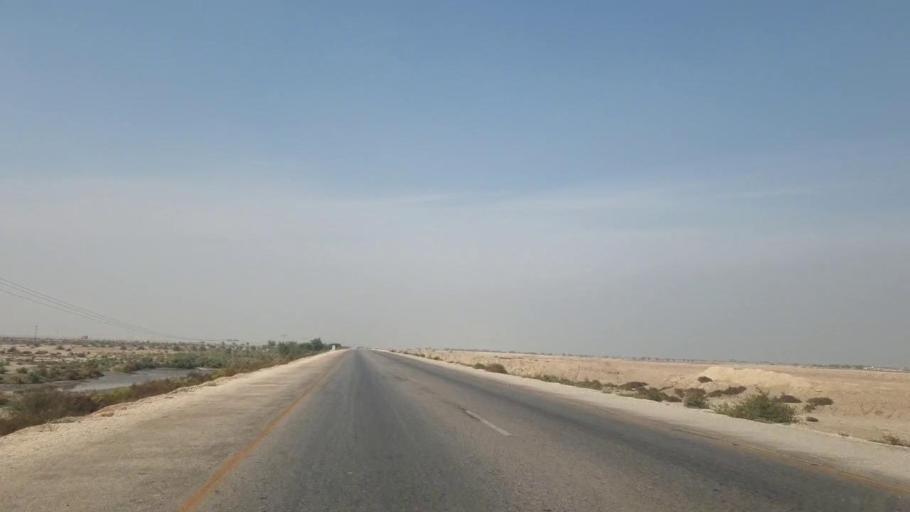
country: PK
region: Sindh
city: Sann
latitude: 25.9047
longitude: 68.2296
